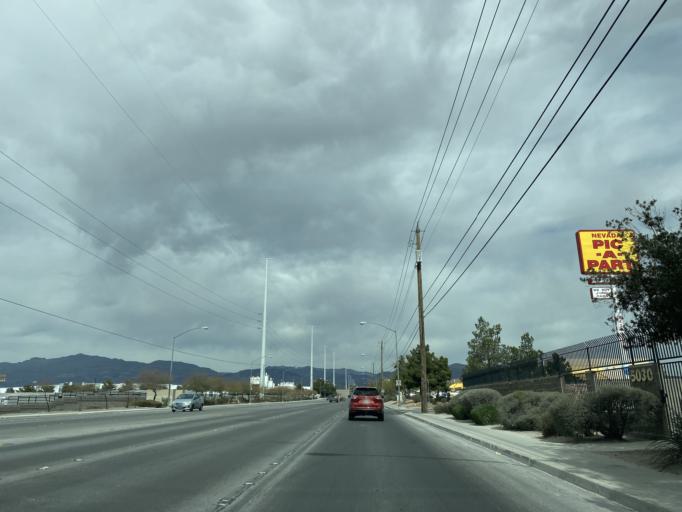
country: US
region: Nevada
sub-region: Clark County
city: Nellis Air Force Base
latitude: 36.2514
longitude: -115.0799
